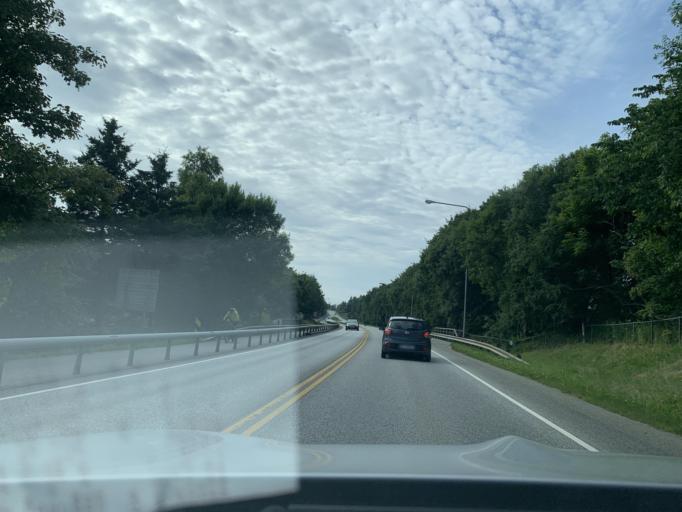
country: NO
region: Rogaland
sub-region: Stavanger
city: Stavanger
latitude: 58.9155
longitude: 5.7217
